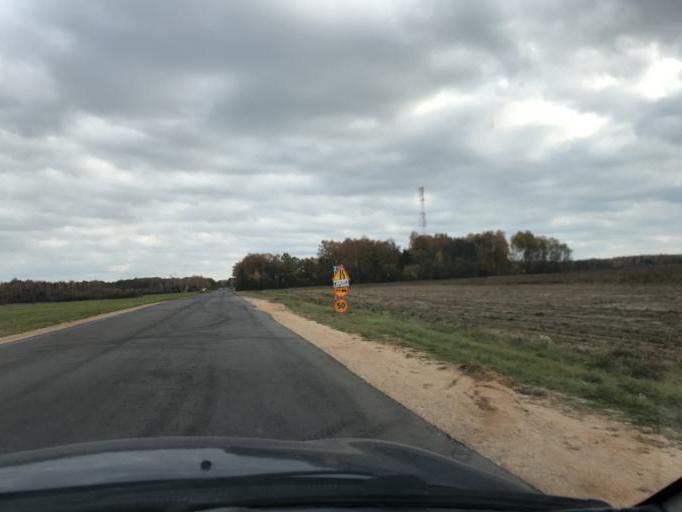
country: BY
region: Grodnenskaya
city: Lida
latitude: 53.7551
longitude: 25.2043
